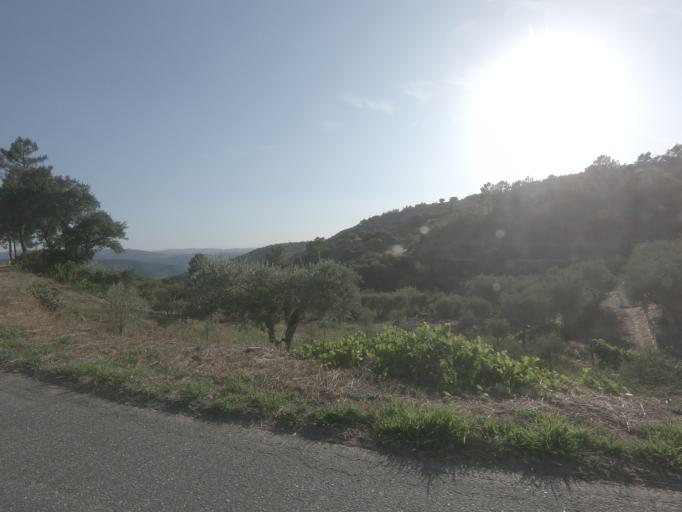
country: PT
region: Vila Real
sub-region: Sabrosa
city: Vilela
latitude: 41.1787
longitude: -7.5970
